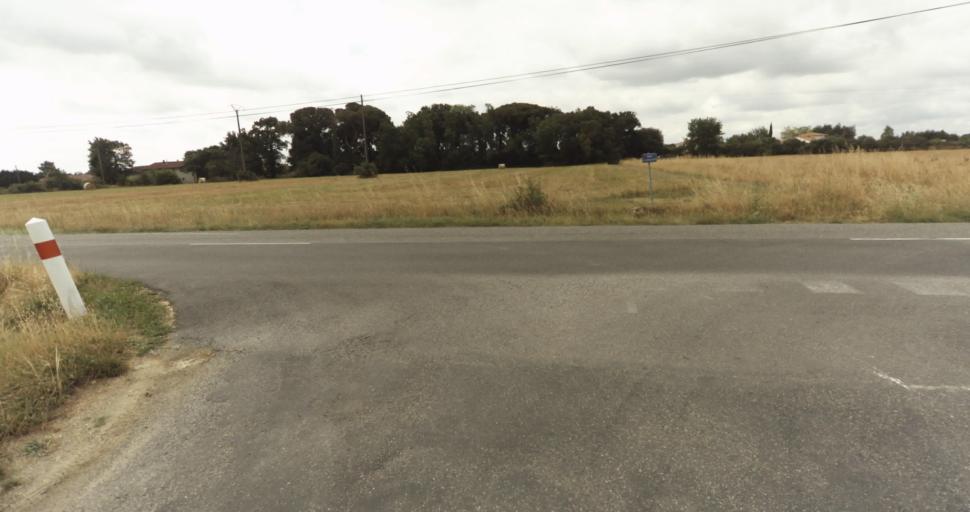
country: FR
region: Midi-Pyrenees
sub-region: Departement de la Haute-Garonne
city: Fonsorbes
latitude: 43.5494
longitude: 1.2136
